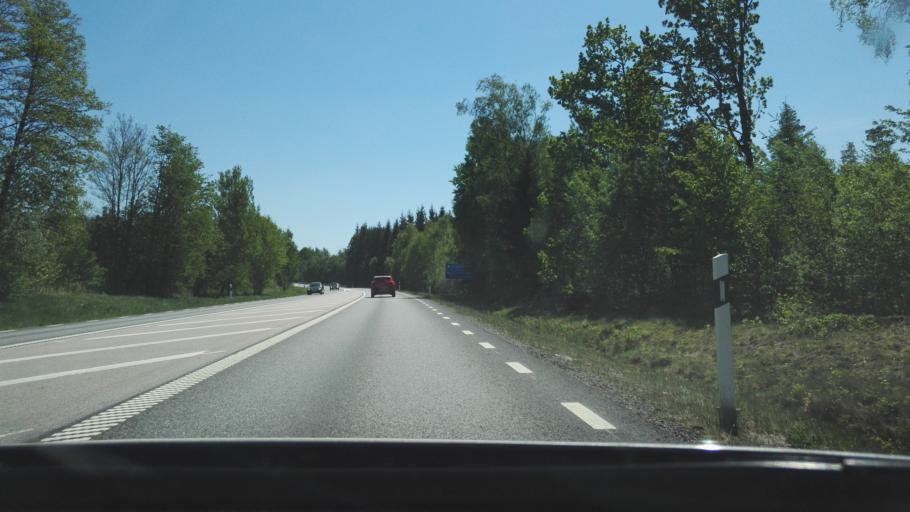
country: SE
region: Kronoberg
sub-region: Tingsryds Kommun
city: Tingsryd
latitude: 56.5908
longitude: 14.9304
